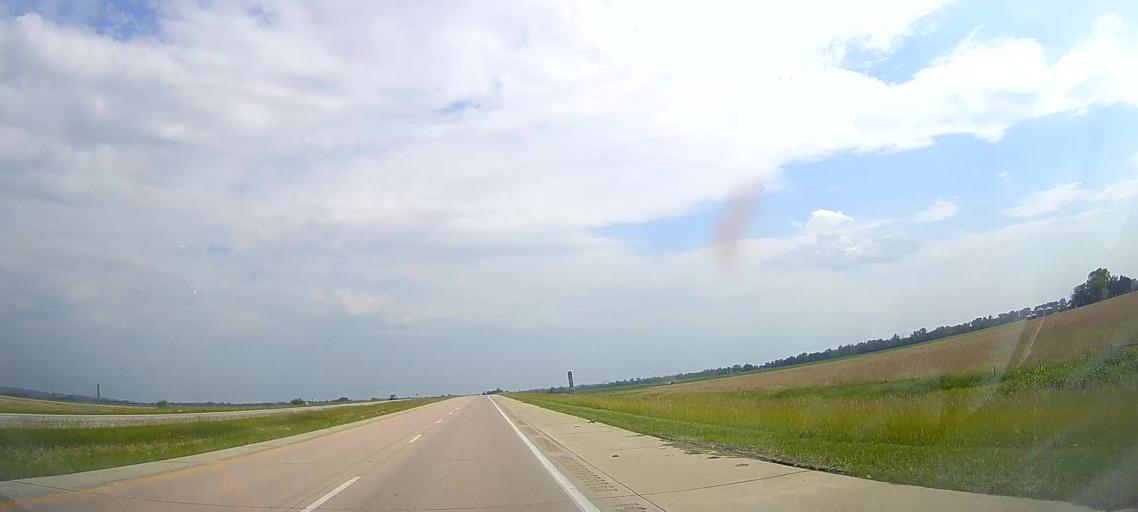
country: US
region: Nebraska
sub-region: Burt County
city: Tekamah
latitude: 41.8685
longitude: -96.1036
